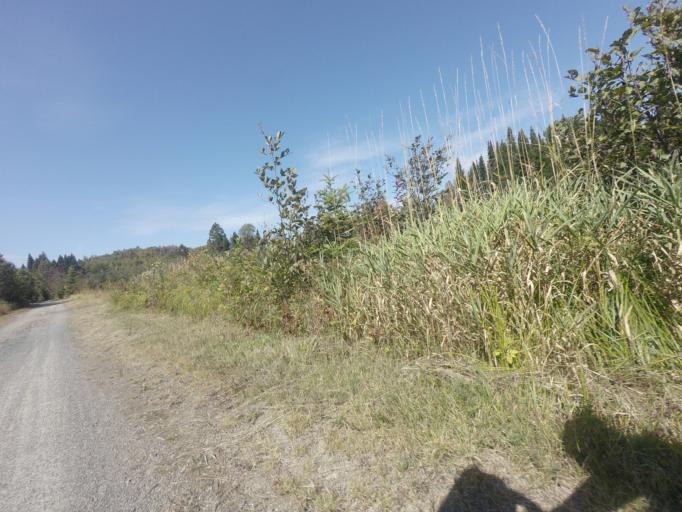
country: CA
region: Quebec
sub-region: Laurentides
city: Sainte-Agathe-des-Monts
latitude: 46.1055
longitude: -74.3996
